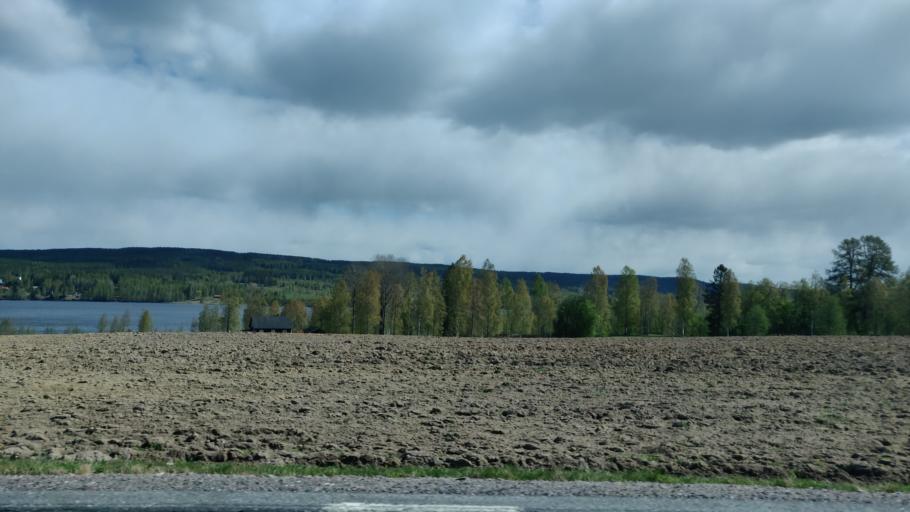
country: SE
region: Vaermland
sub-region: Munkfors Kommun
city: Munkfors
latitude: 59.8566
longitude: 13.7063
